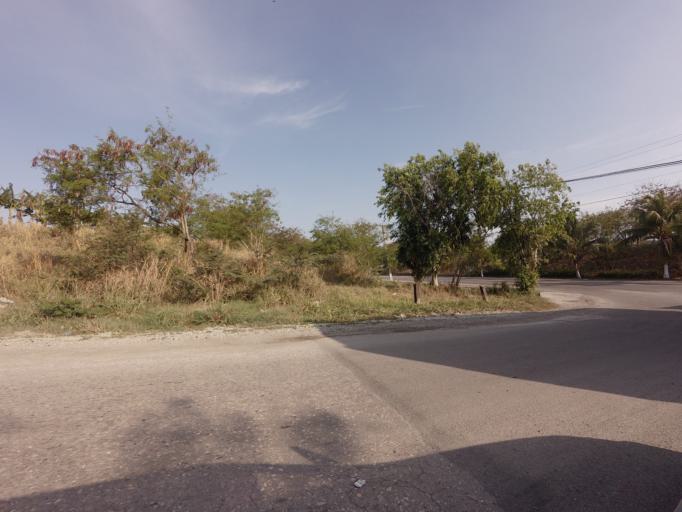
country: CU
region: La Habana
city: Regla
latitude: 23.1103
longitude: -82.3410
